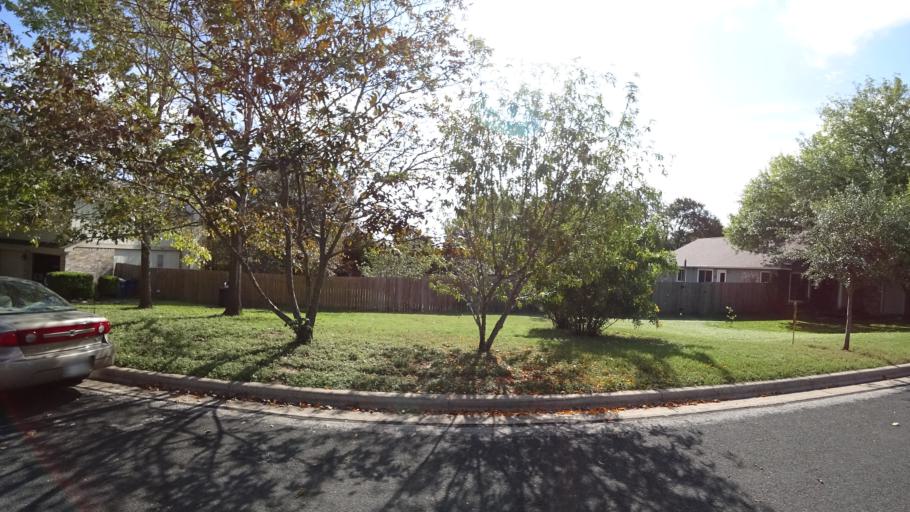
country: US
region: Texas
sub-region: Travis County
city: Shady Hollow
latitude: 30.1945
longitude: -97.8264
